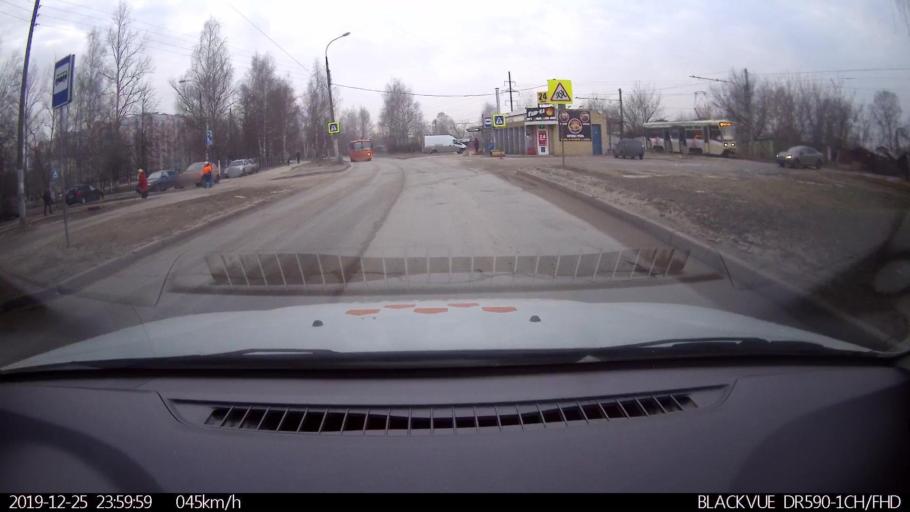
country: RU
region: Nizjnij Novgorod
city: Gorbatovka
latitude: 56.2633
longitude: 43.8480
